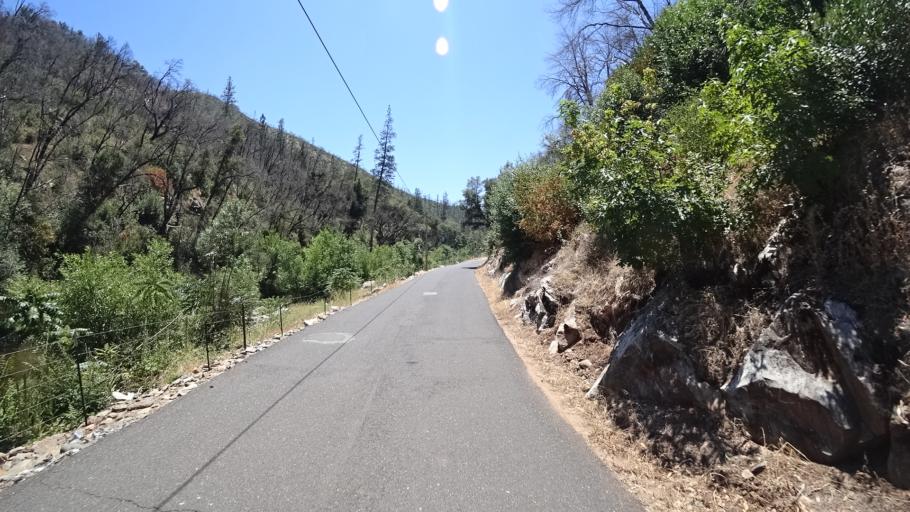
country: US
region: California
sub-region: Calaveras County
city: San Andreas
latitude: 38.2862
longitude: -120.6644
